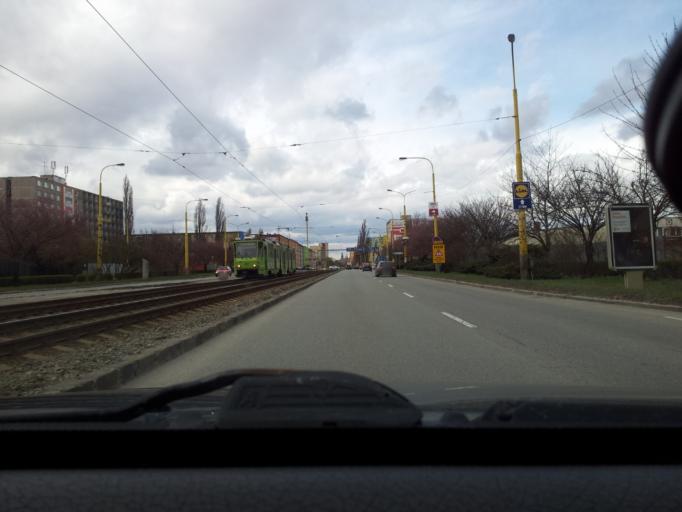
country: SK
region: Kosicky
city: Kosice
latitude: 48.7021
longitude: 21.2629
